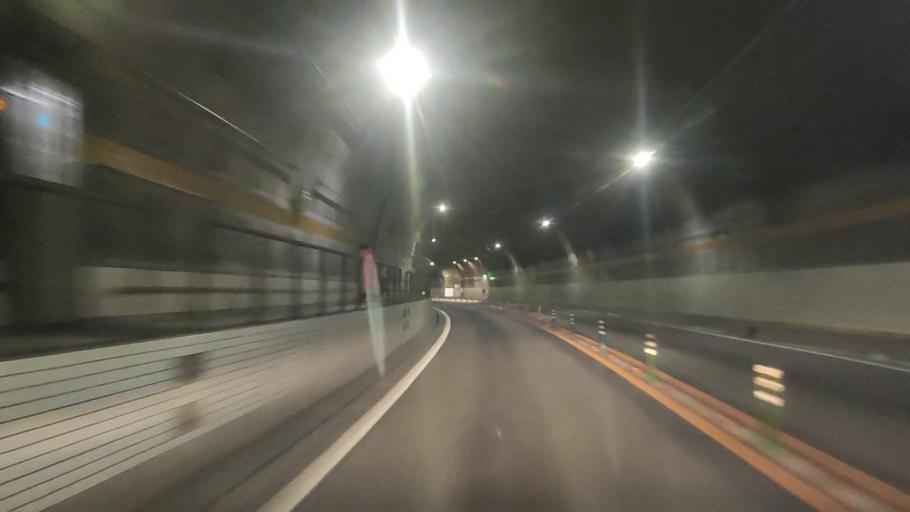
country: JP
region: Nagasaki
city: Obita
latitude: 32.7904
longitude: 129.8813
